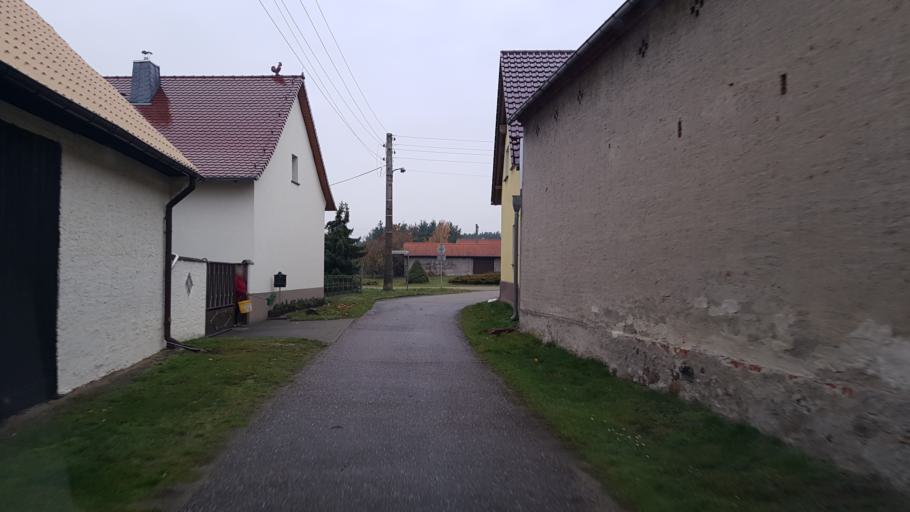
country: DE
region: Brandenburg
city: Schilda
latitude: 51.6444
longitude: 13.3867
